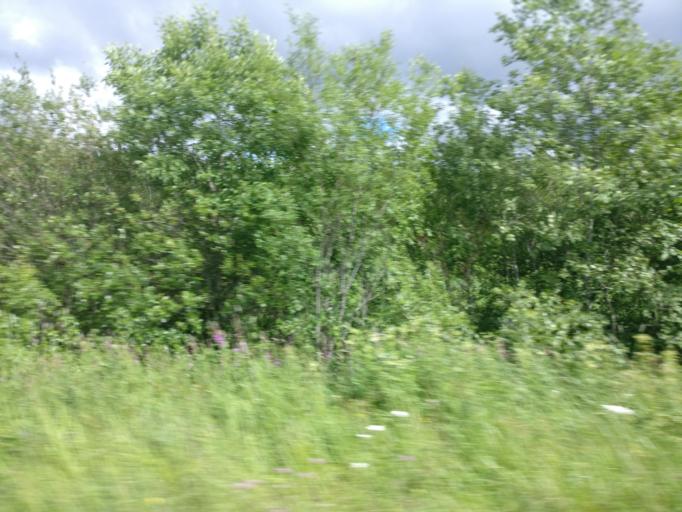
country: FI
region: Northern Savo
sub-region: Koillis-Savo
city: Juankoski
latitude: 62.9288
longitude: 28.2132
